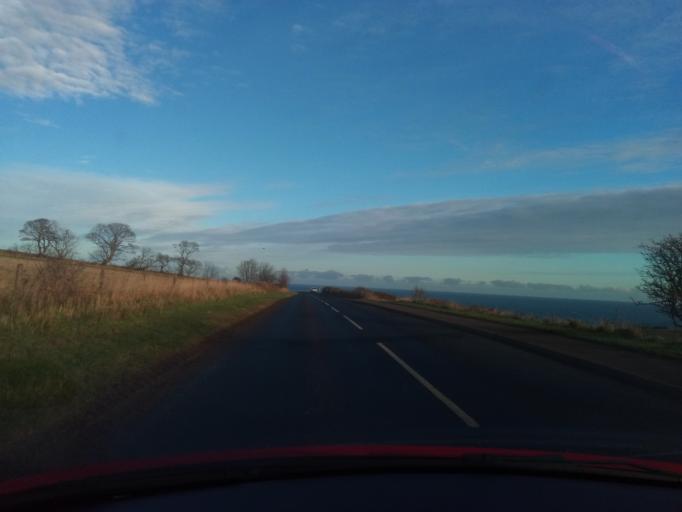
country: GB
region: Scotland
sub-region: The Scottish Borders
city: Eyemouth
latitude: 55.8911
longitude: -2.1487
